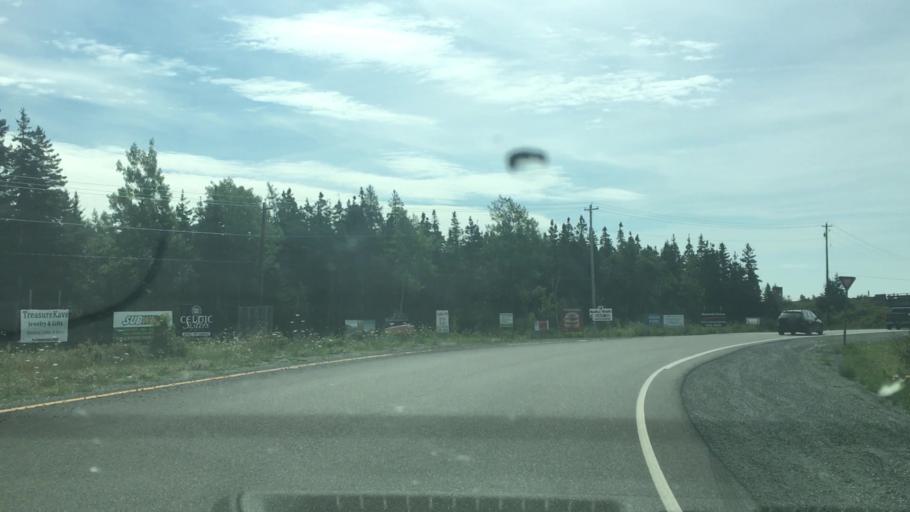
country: CA
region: Nova Scotia
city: Port Hawkesbury
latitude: 45.6267
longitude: -61.3322
